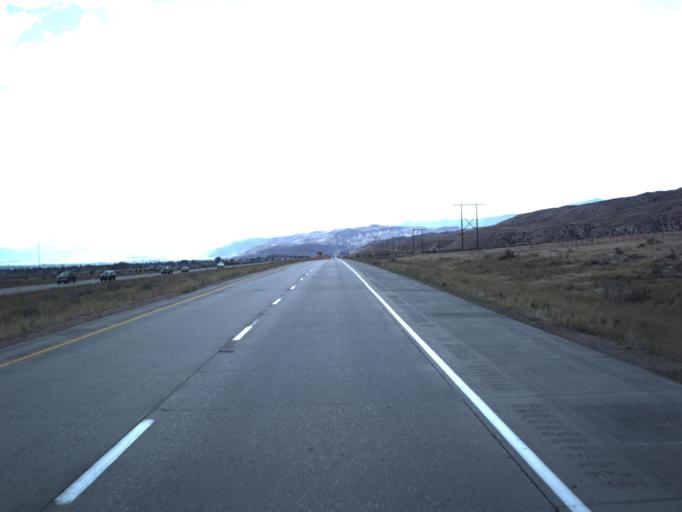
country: US
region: Utah
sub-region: Sevier County
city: Richfield
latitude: 38.8185
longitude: -112.0490
